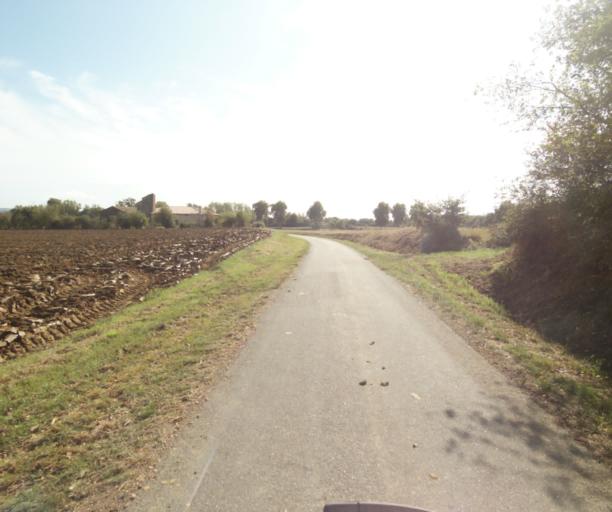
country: FR
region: Midi-Pyrenees
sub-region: Departement du Tarn-et-Garonne
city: Verdun-sur-Garonne
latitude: 43.8461
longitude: 1.1985
